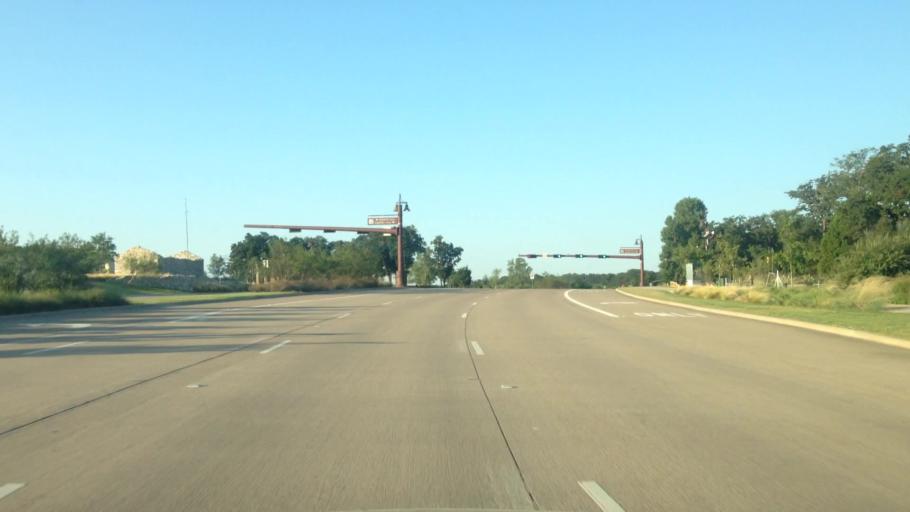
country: US
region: Texas
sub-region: Denton County
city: Trophy Club
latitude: 32.9874
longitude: -97.1826
